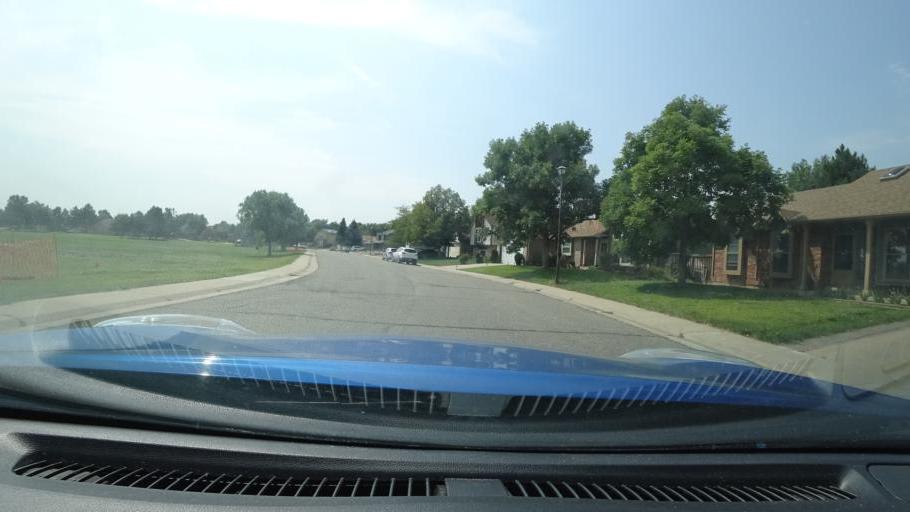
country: US
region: Colorado
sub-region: Adams County
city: Aurora
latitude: 39.7813
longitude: -104.7632
